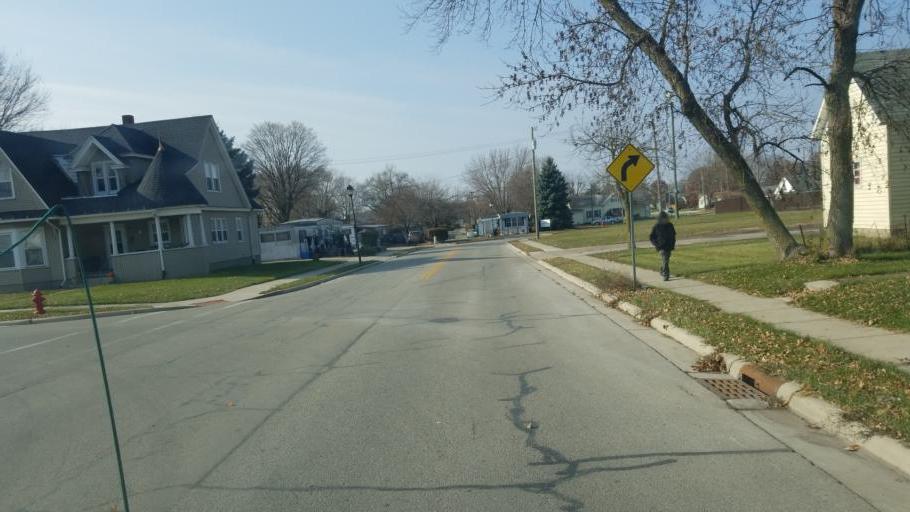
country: US
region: Ohio
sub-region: Mercer County
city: Celina
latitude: 40.5567
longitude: -84.5749
